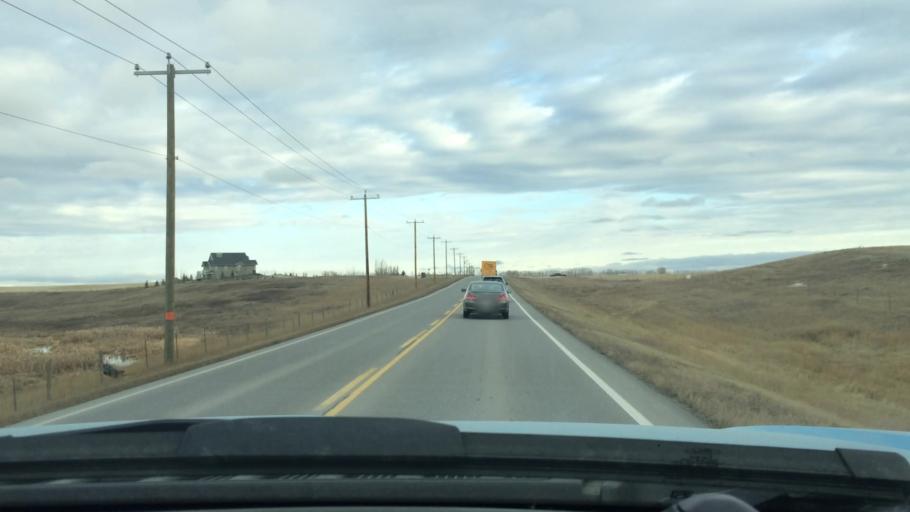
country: CA
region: Alberta
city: Airdrie
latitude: 51.2166
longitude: -114.0249
